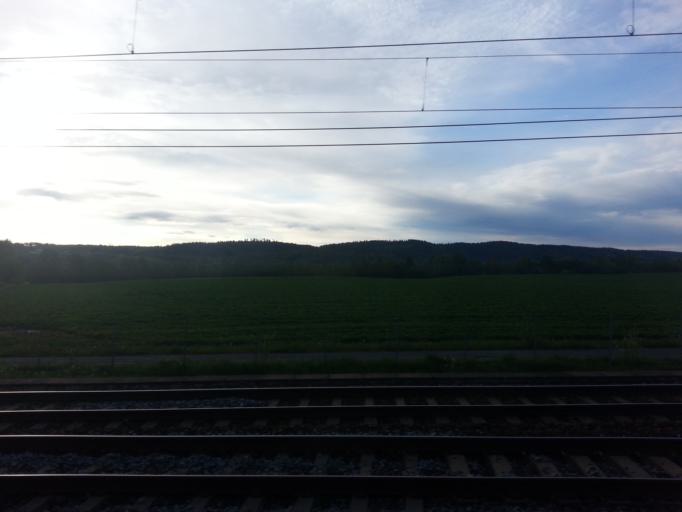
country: NO
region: Akershus
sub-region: Skedsmo
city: Leirsund
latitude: 59.9768
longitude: 11.0709
